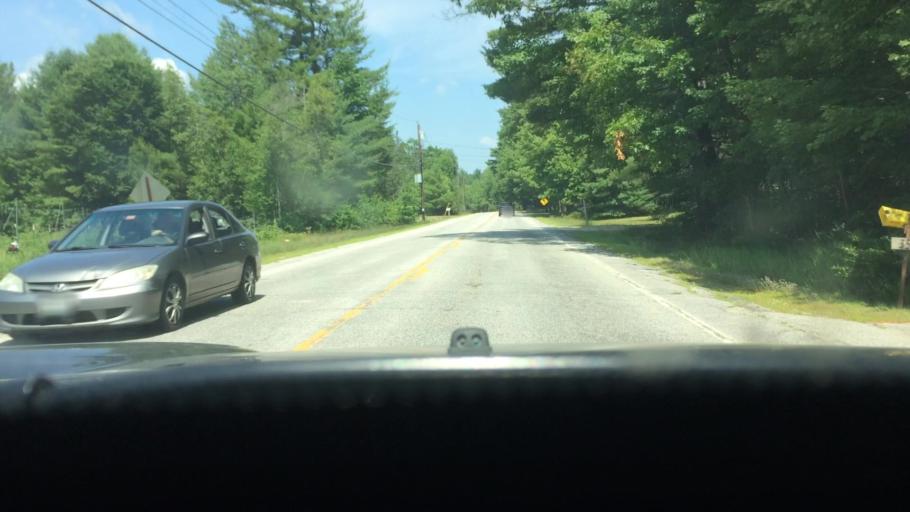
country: US
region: Maine
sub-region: Androscoggin County
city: Mechanic Falls
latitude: 44.1124
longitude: -70.4225
